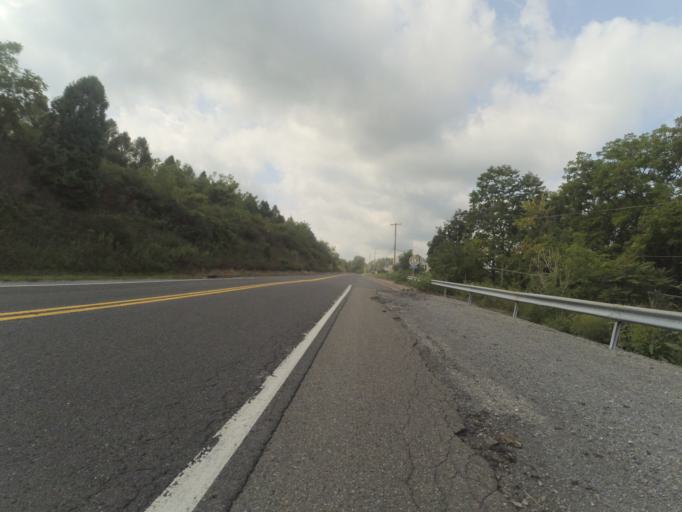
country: US
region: Pennsylvania
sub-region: Centre County
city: Bellefonte
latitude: 40.9191
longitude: -77.7636
